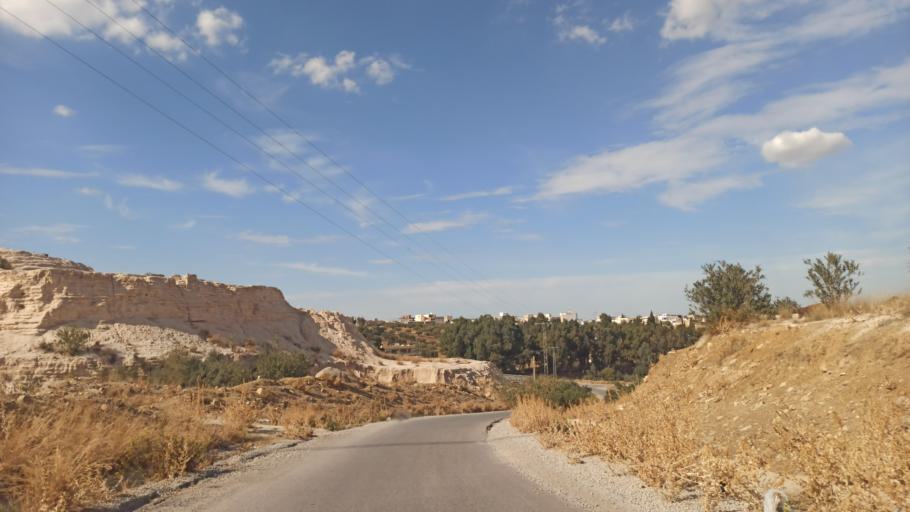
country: TN
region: Zaghwan
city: Zaghouan
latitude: 36.3424
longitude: 10.2078
